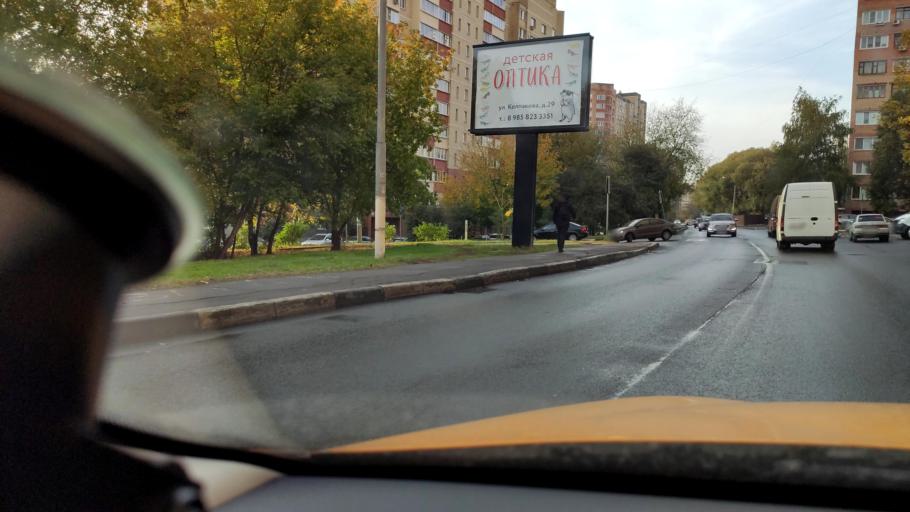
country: RU
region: Moskovskaya
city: Mytishchi
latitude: 55.9182
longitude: 37.7312
